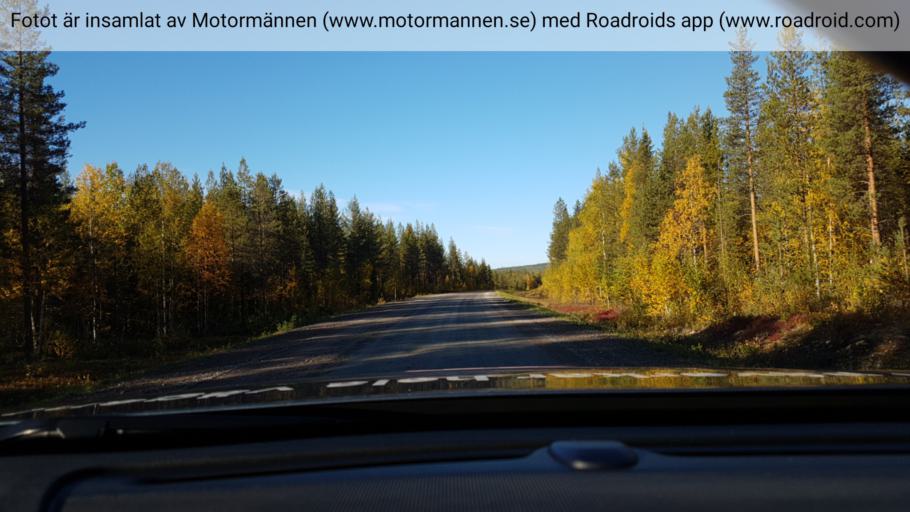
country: SE
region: Norrbotten
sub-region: Alvsbyns Kommun
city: AElvsbyn
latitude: 66.2649
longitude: 21.0448
